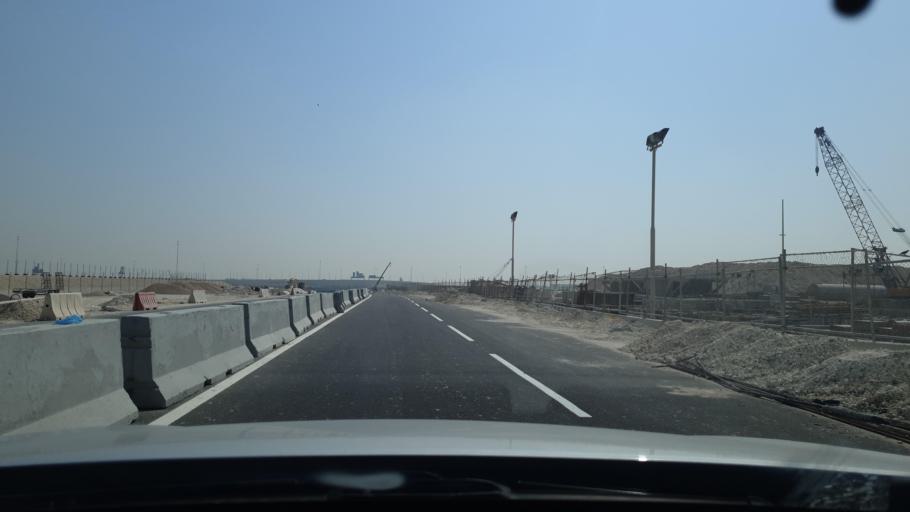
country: QA
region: Baladiyat ad Dawhah
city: Doha
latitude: 25.2240
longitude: 51.5232
